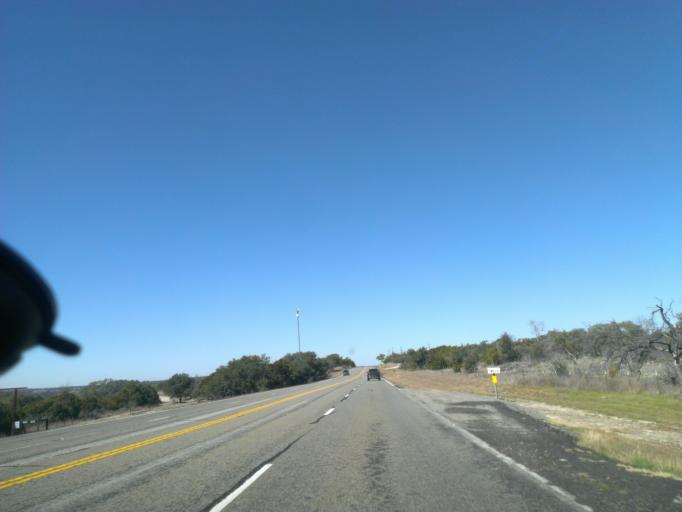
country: US
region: Texas
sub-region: Lampasas County
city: Kempner
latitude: 30.9176
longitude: -97.9801
